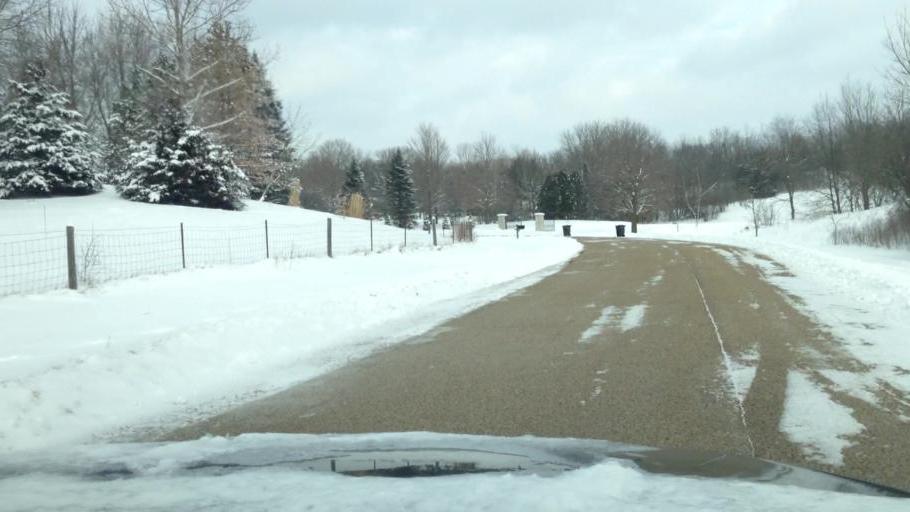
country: US
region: Wisconsin
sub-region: Waukesha County
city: North Prairie
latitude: 42.9461
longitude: -88.4158
